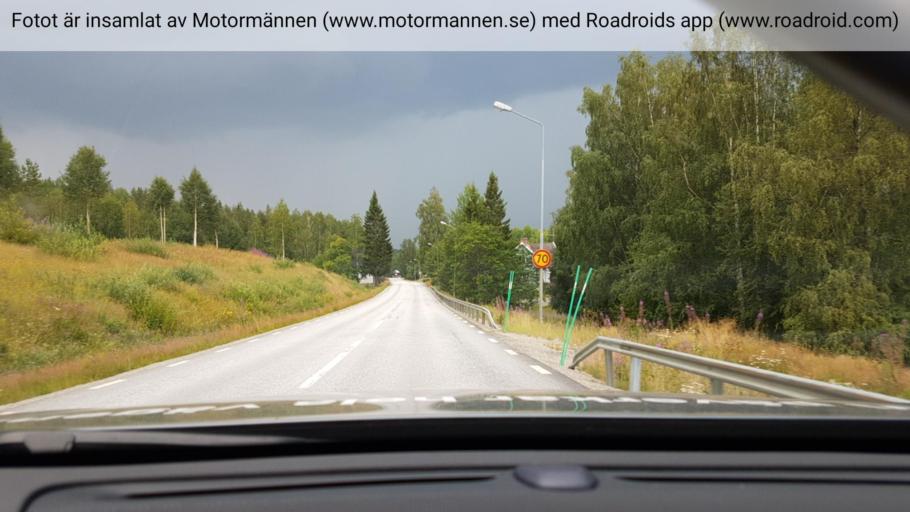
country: SE
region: Vaesterbotten
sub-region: Vindelns Kommun
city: Vindeln
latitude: 64.1562
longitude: 19.5068
